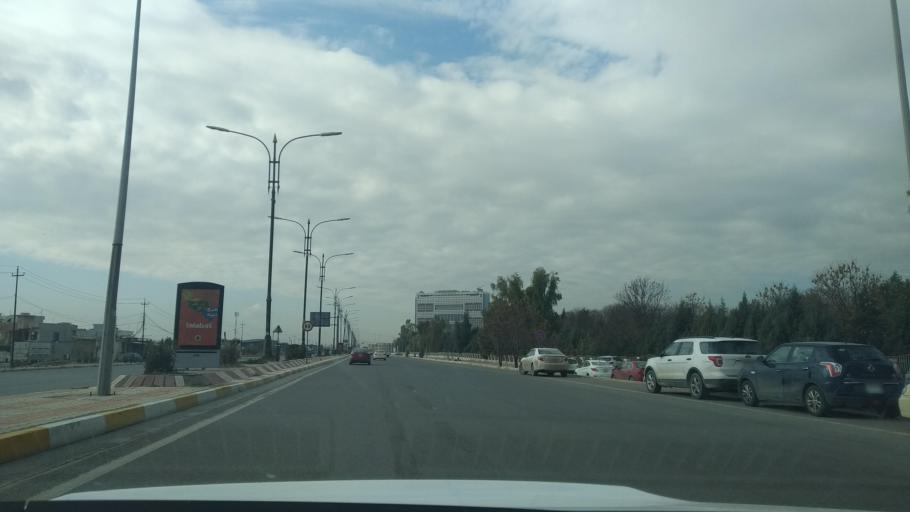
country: IQ
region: Arbil
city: Erbil
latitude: 36.1894
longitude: 43.9918
